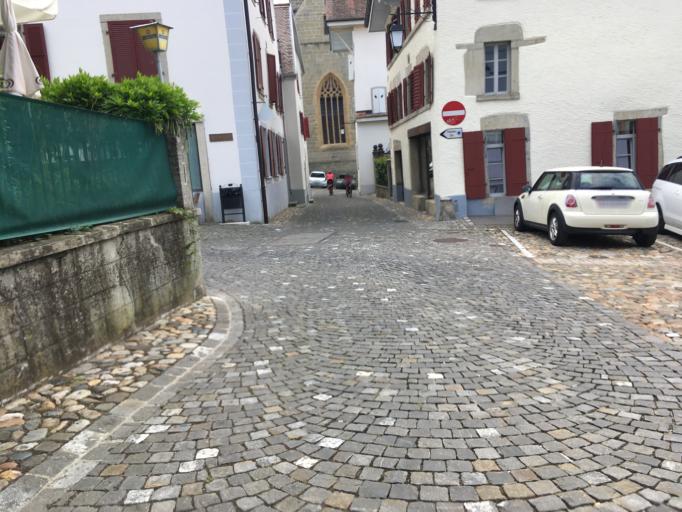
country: CH
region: Fribourg
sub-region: Broye District
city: Estavayer-le-Lac
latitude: 46.8505
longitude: 6.8478
